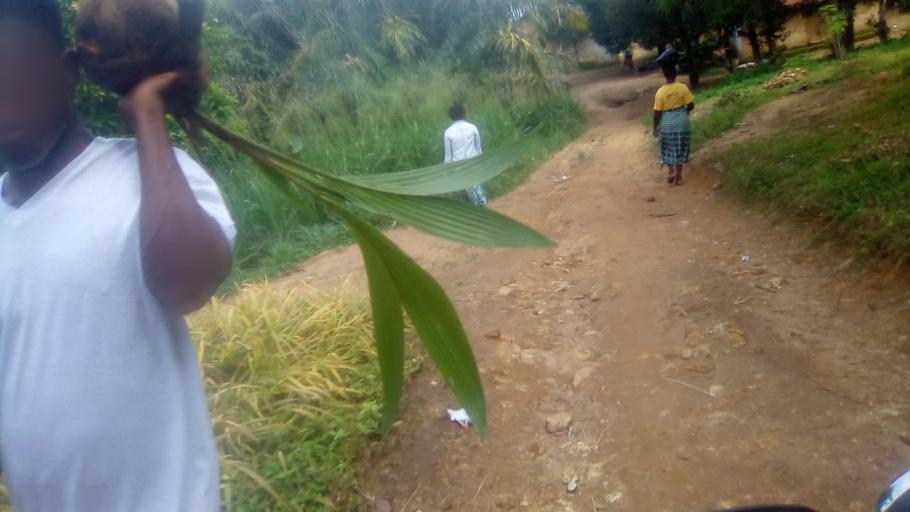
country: SL
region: Eastern Province
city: Kailahun
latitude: 8.2853
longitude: -10.5619
